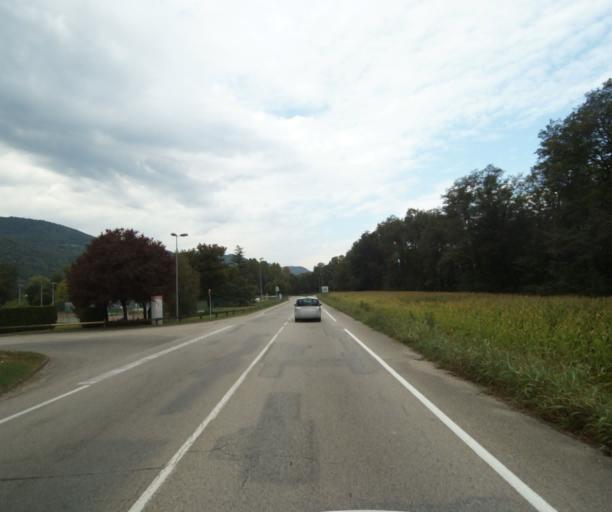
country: FR
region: Rhone-Alpes
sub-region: Departement de l'Isere
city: Domene
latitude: 45.2068
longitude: 5.8271
